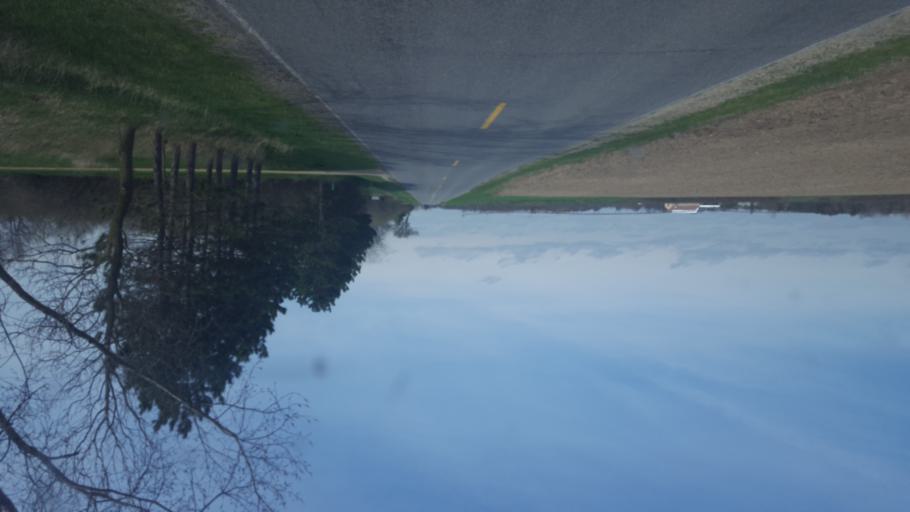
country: US
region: Michigan
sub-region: Montcalm County
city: Edmore
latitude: 43.4172
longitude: -85.0049
